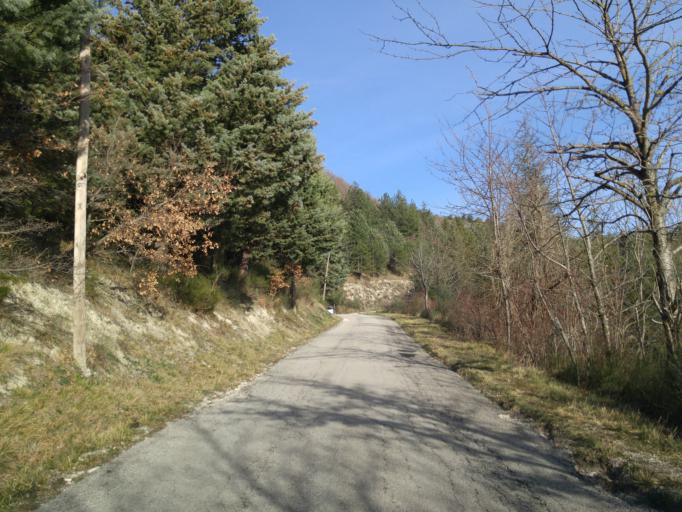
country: IT
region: The Marches
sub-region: Provincia di Pesaro e Urbino
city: Fermignano
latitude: 43.6779
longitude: 12.6725
